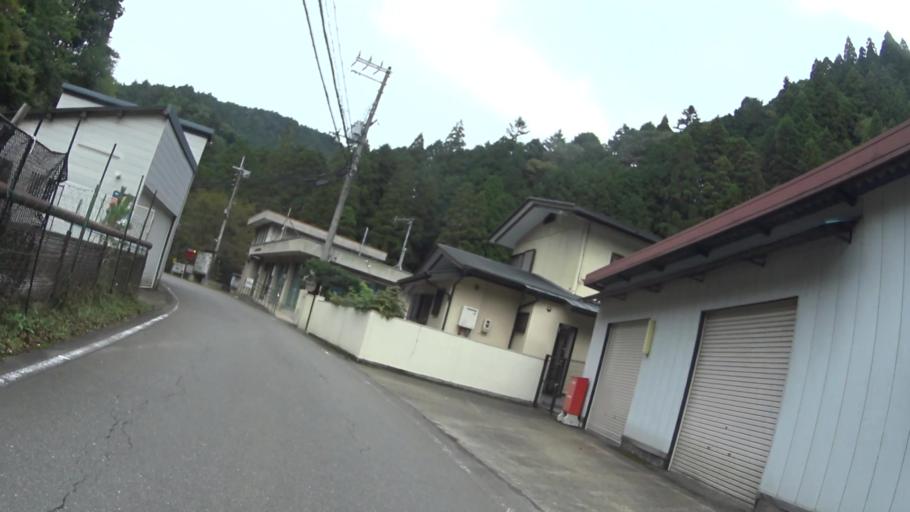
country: JP
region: Shiga Prefecture
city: Kitahama
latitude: 35.2089
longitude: 135.7760
